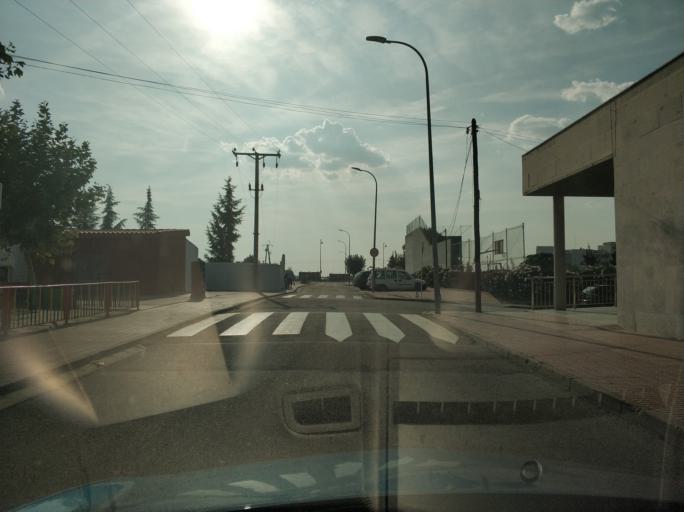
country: ES
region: Castille and Leon
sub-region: Provincia de Salamanca
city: Santa Marta de Tormes
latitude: 40.9476
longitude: -5.6262
